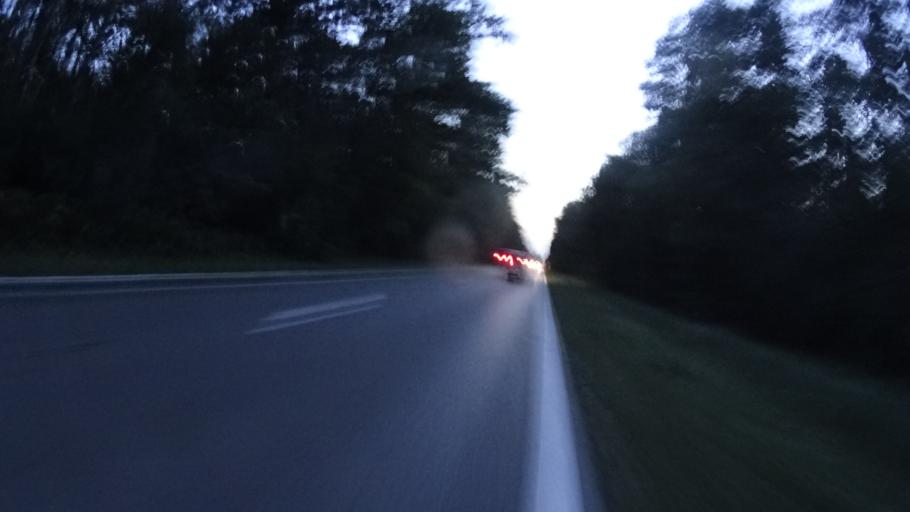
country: PL
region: Masovian Voivodeship
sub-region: Powiat warszawski zachodni
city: Leszno
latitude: 52.2634
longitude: 20.6590
